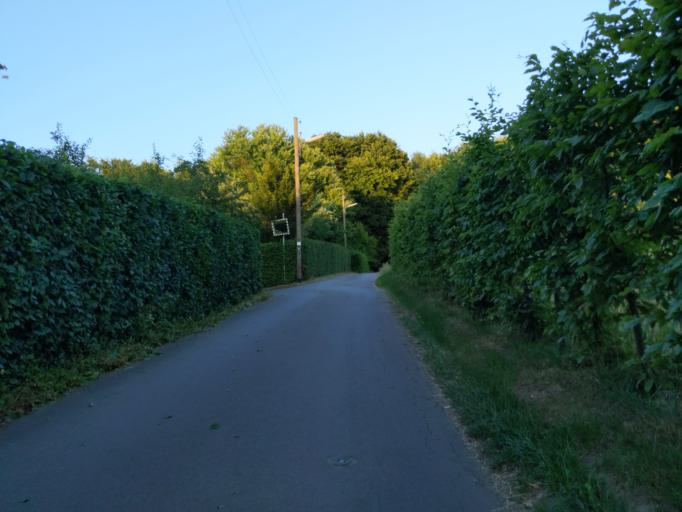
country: DE
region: North Rhine-Westphalia
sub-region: Regierungsbezirk Detmold
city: Bielefeld
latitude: 52.0234
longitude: 8.4932
